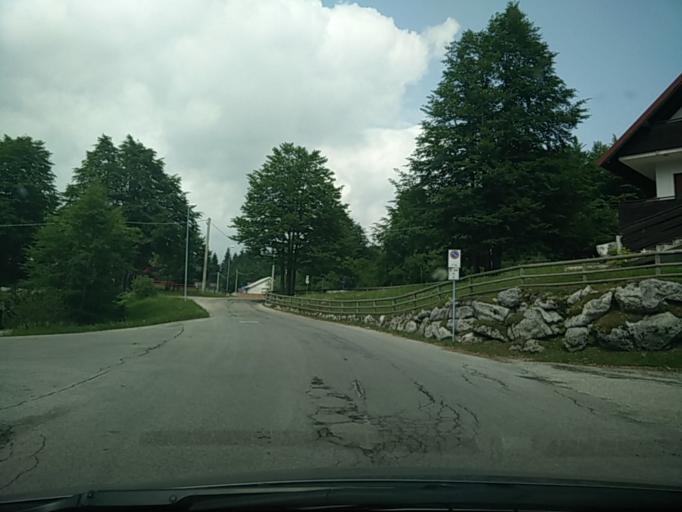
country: IT
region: Friuli Venezia Giulia
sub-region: Provincia di Pordenone
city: Budoia
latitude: 46.1092
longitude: 12.5228
